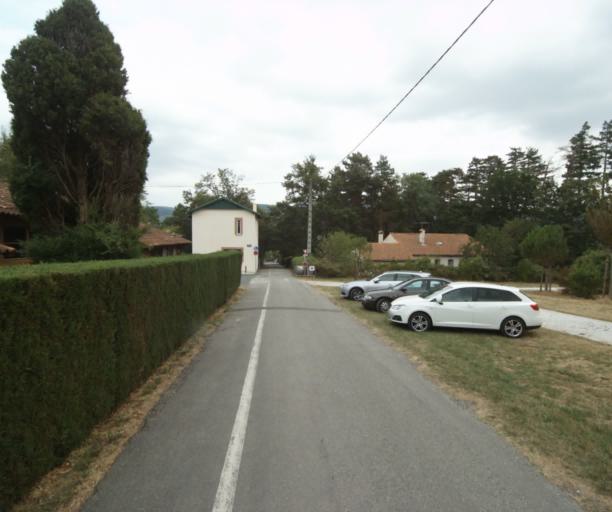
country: FR
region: Midi-Pyrenees
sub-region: Departement de la Haute-Garonne
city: Revel
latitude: 43.4404
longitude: 2.0199
